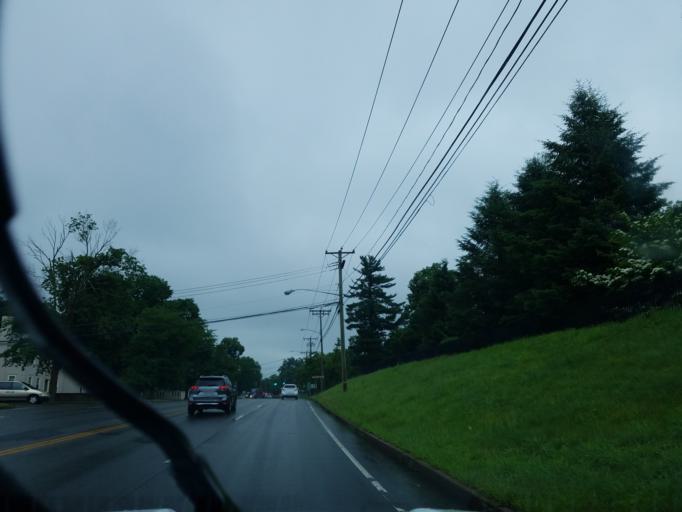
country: US
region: Connecticut
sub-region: Middlesex County
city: Middletown
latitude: 41.5584
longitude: -72.6634
